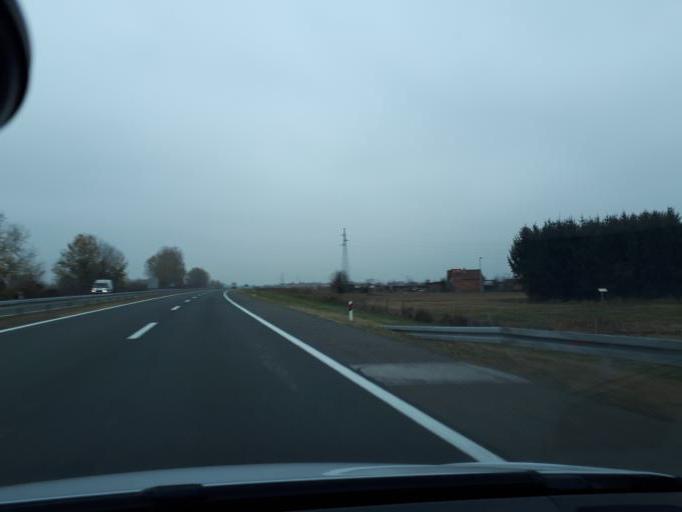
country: HR
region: Brodsko-Posavska
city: Podvinje
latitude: 45.1842
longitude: 18.0333
